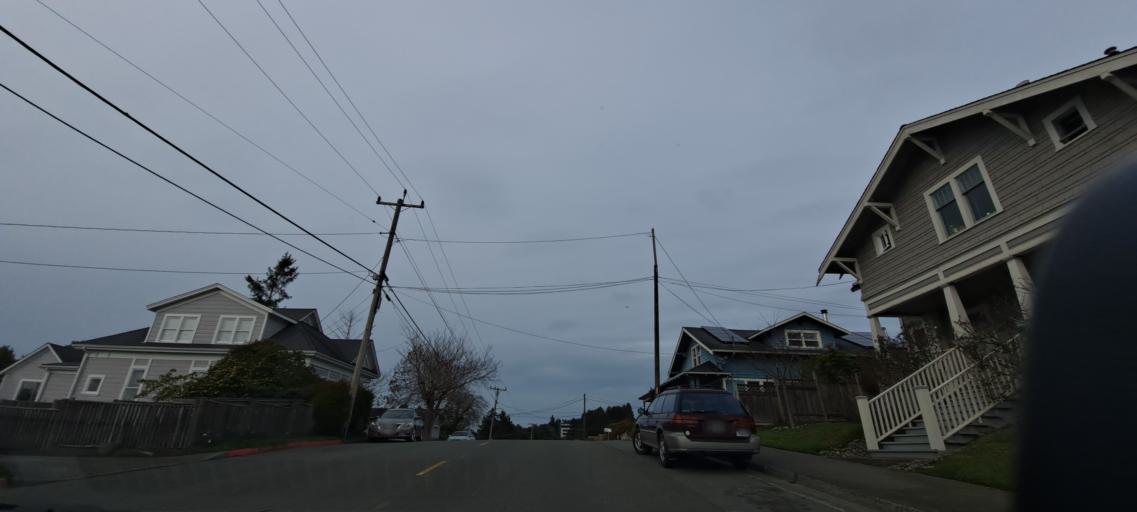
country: US
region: California
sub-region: Humboldt County
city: Arcata
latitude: 40.8673
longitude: -124.0779
